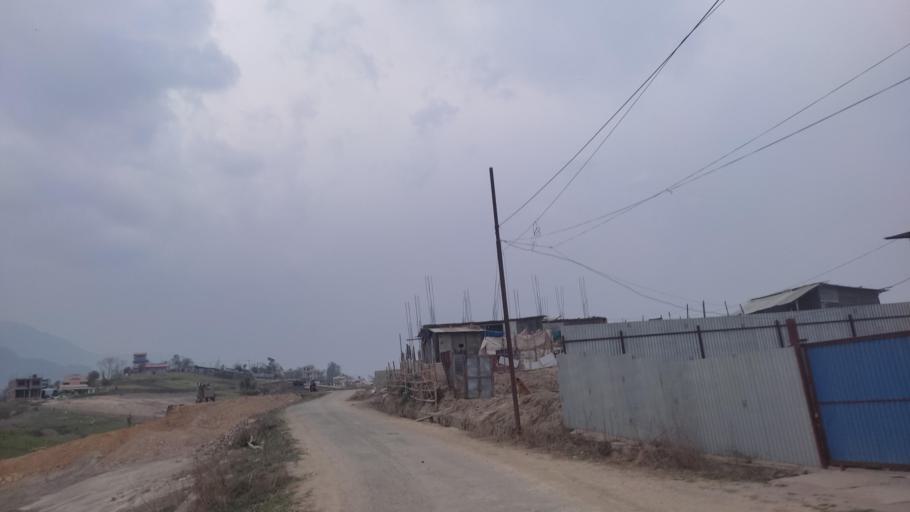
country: NP
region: Central Region
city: Kirtipur
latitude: 27.6596
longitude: 85.2854
